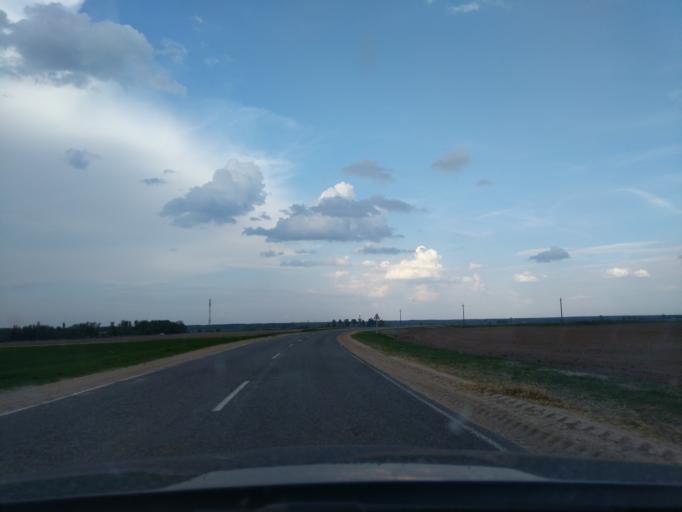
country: BY
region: Grodnenskaya
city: Lyubcha
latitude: 53.7503
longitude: 26.0230
